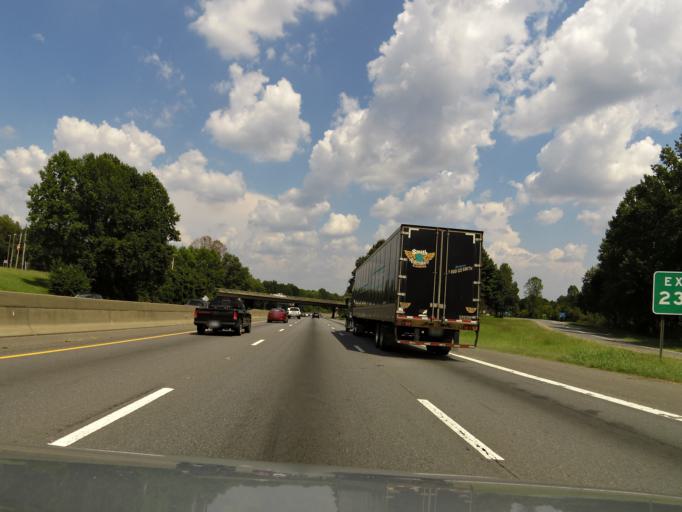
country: US
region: North Carolina
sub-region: Gaston County
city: Lowell
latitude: 35.2630
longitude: -81.0908
